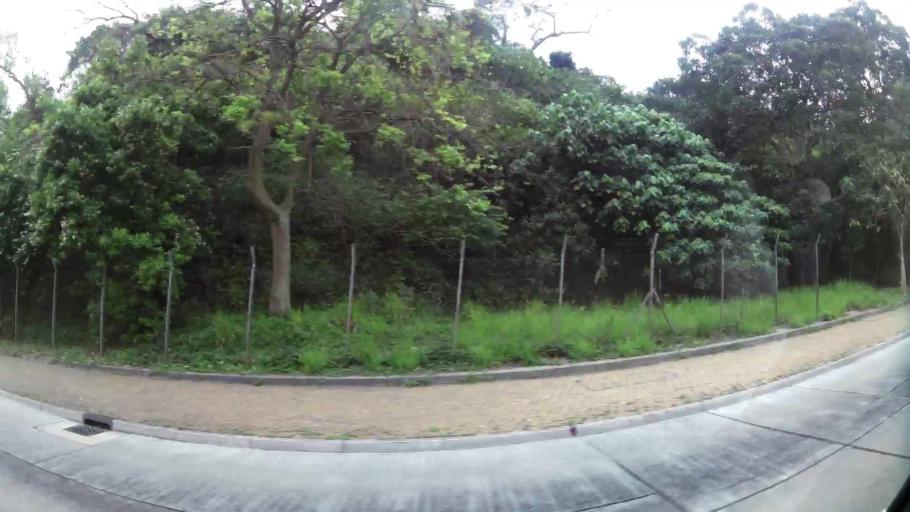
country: HK
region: Wanchai
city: Wan Chai
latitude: 22.2724
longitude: 114.2329
